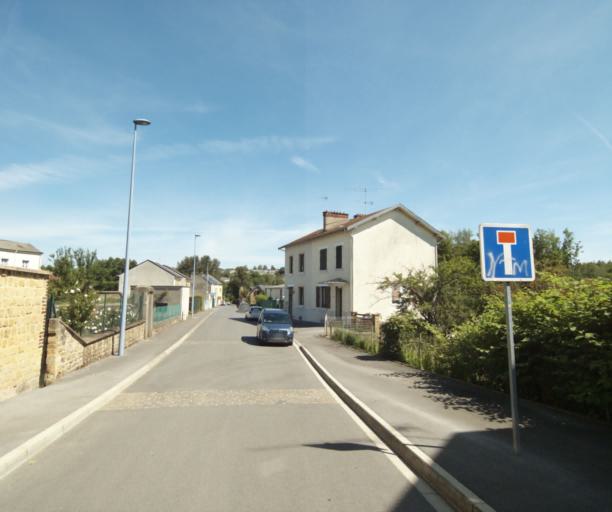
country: FR
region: Champagne-Ardenne
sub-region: Departement des Ardennes
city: Villers-Semeuse
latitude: 49.7536
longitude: 4.7325
